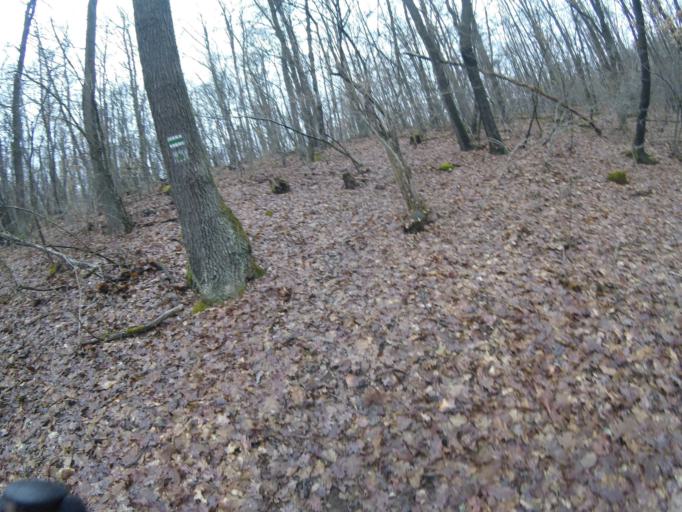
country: HU
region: Borsod-Abauj-Zemplen
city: Rudabanya
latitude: 48.4553
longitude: 20.5703
